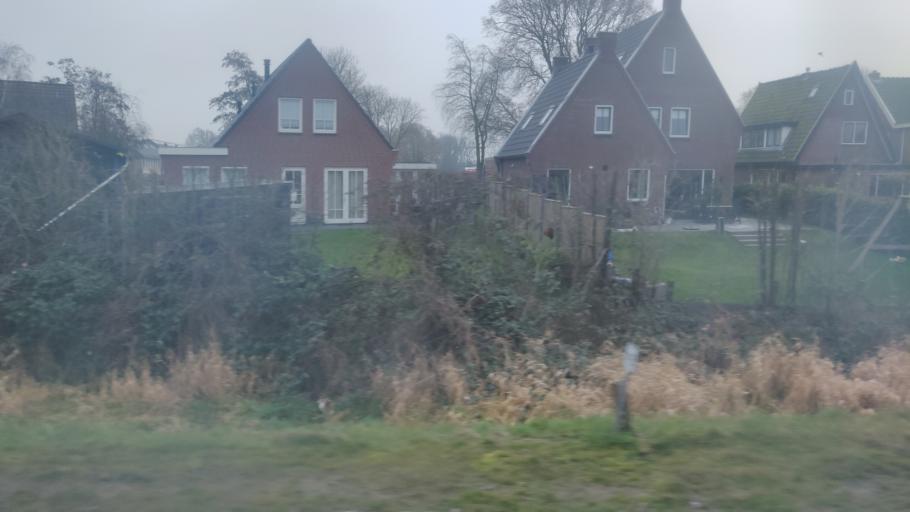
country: NL
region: North Holland
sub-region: Gemeente Heiloo
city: Heiloo
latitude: 52.5938
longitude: 4.6955
